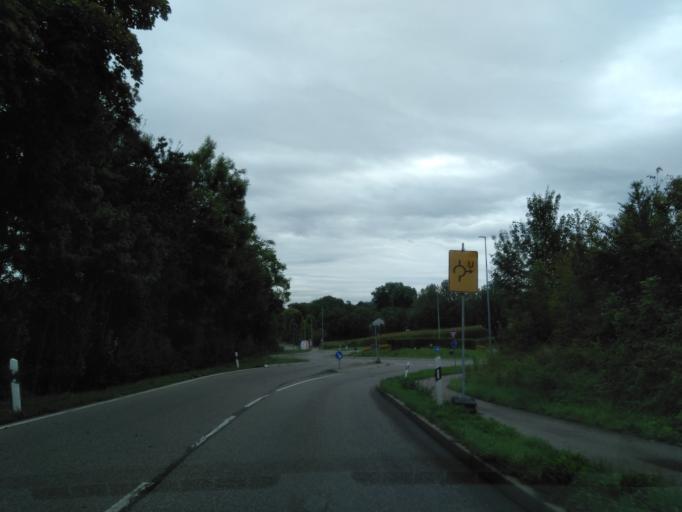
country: DE
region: Baden-Wuerttemberg
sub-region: Regierungsbezirk Stuttgart
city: Markgroningen
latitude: 48.9089
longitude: 9.0916
